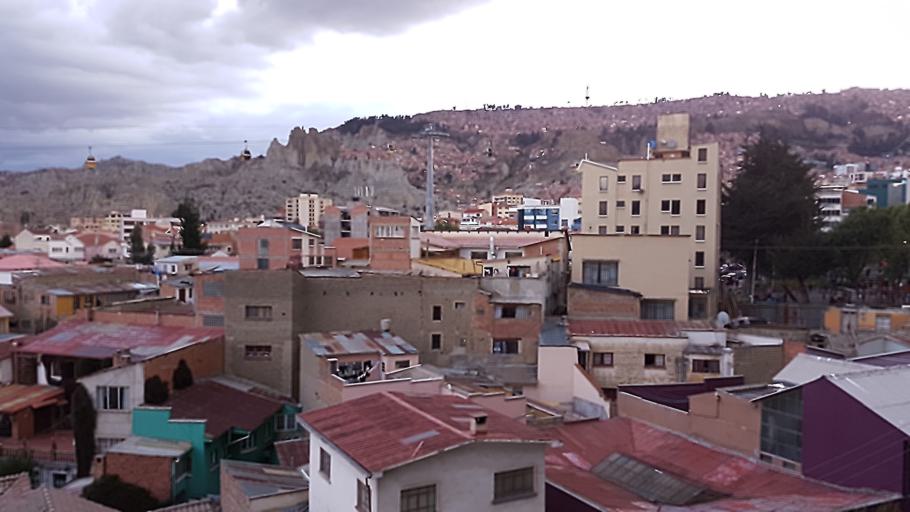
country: BO
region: La Paz
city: La Paz
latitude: -16.5141
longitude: -68.1272
